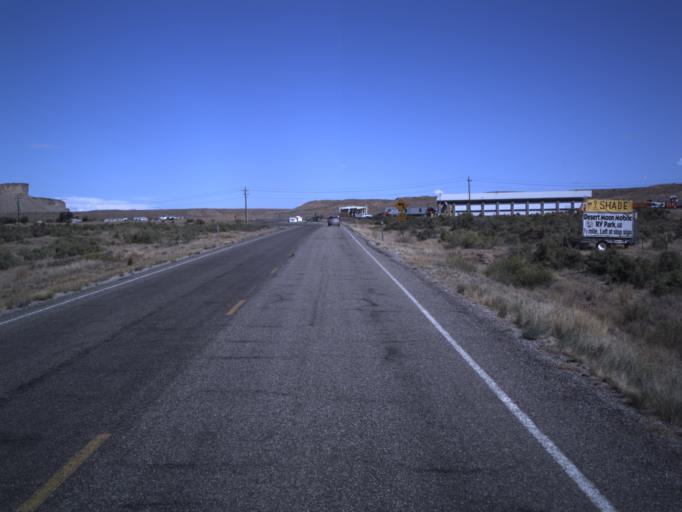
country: US
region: Utah
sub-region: Grand County
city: Moab
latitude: 38.9659
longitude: -109.7189
